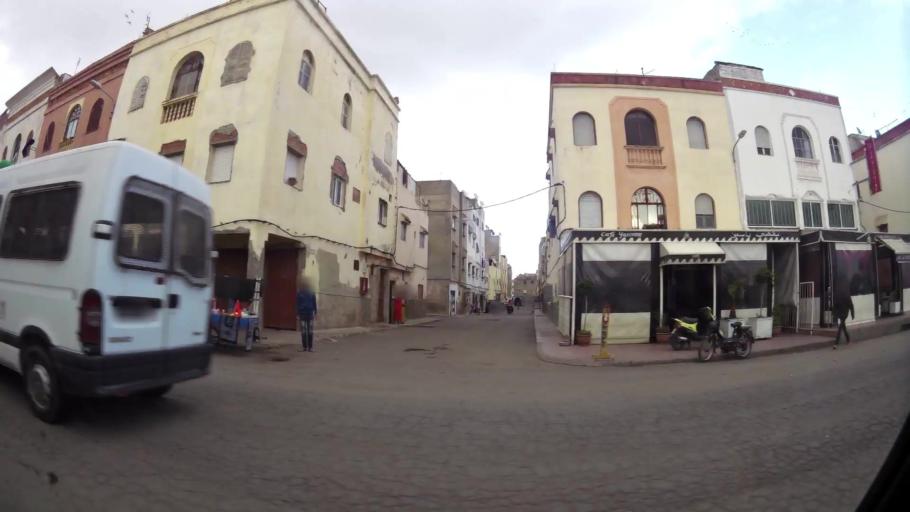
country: MA
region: Grand Casablanca
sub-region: Casablanca
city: Casablanca
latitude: 33.5580
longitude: -7.6926
